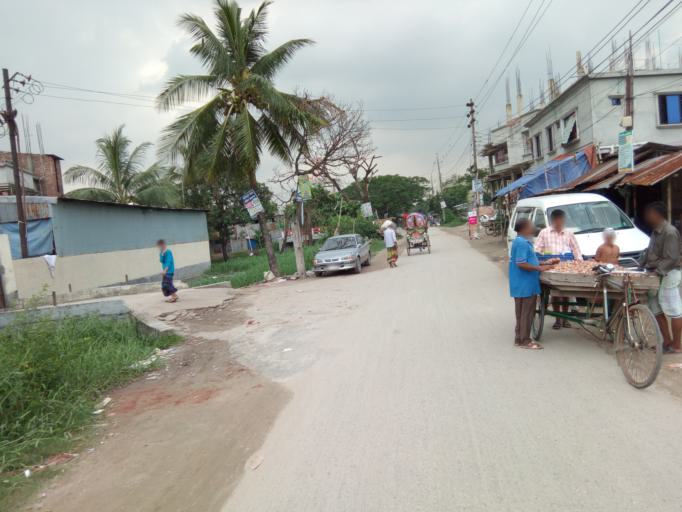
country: BD
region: Dhaka
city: Paltan
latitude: 23.7085
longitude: 90.4862
